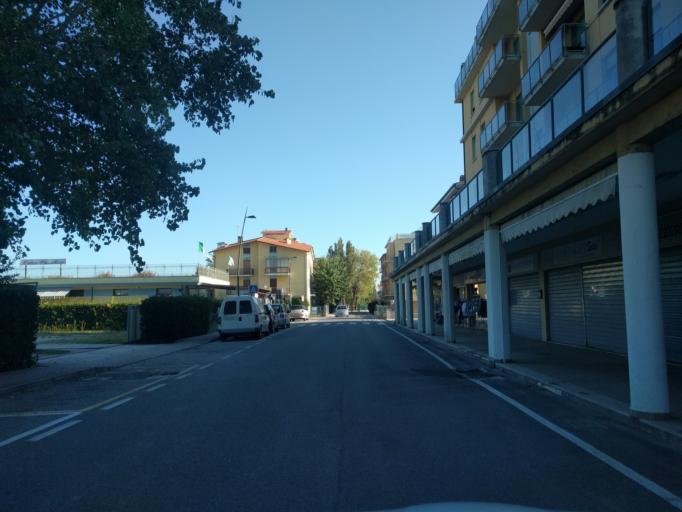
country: IT
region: The Marches
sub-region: Provincia di Pesaro e Urbino
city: Marotta
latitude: 43.8003
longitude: 13.0932
